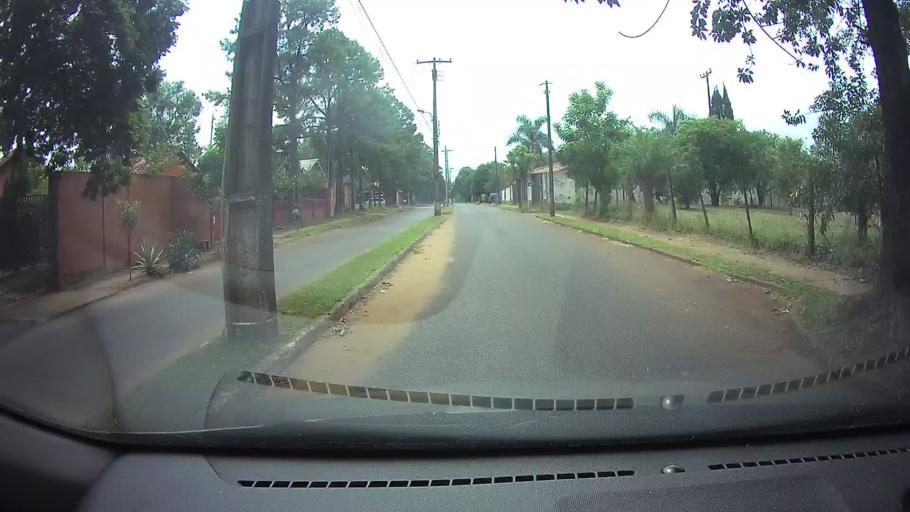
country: PY
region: Central
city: San Lorenzo
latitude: -25.2909
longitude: -57.5110
